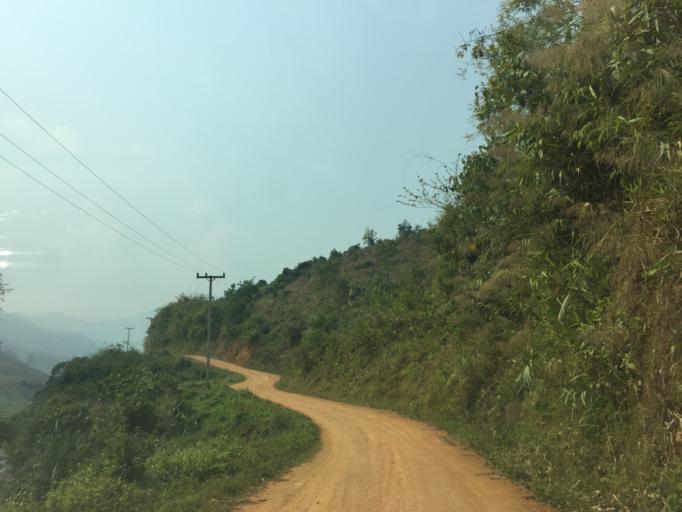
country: TH
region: Phayao
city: Phu Sang
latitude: 19.5799
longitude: 100.5278
